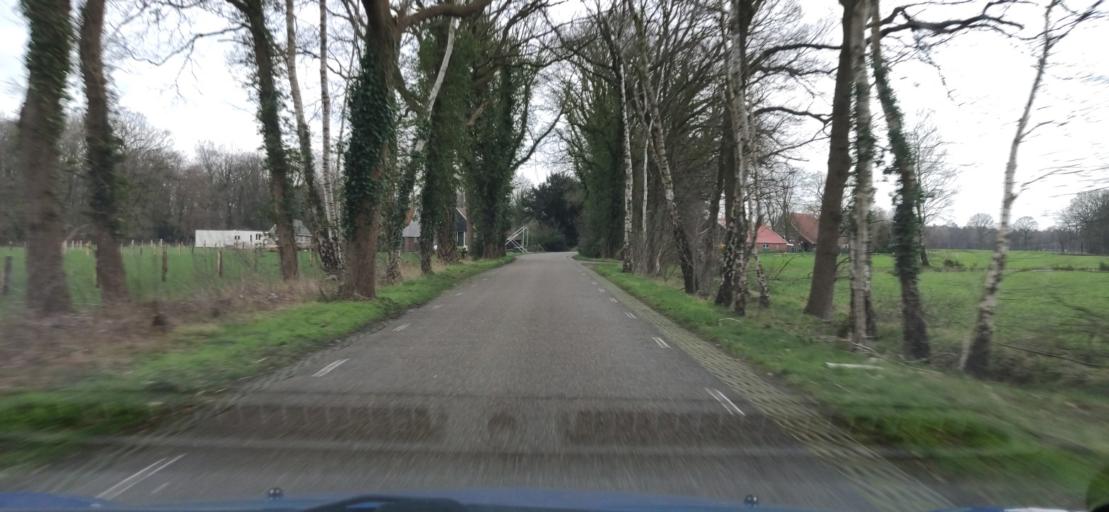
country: NL
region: Overijssel
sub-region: Gemeente Hengelo
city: Hengelo
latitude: 52.2245
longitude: 6.7692
